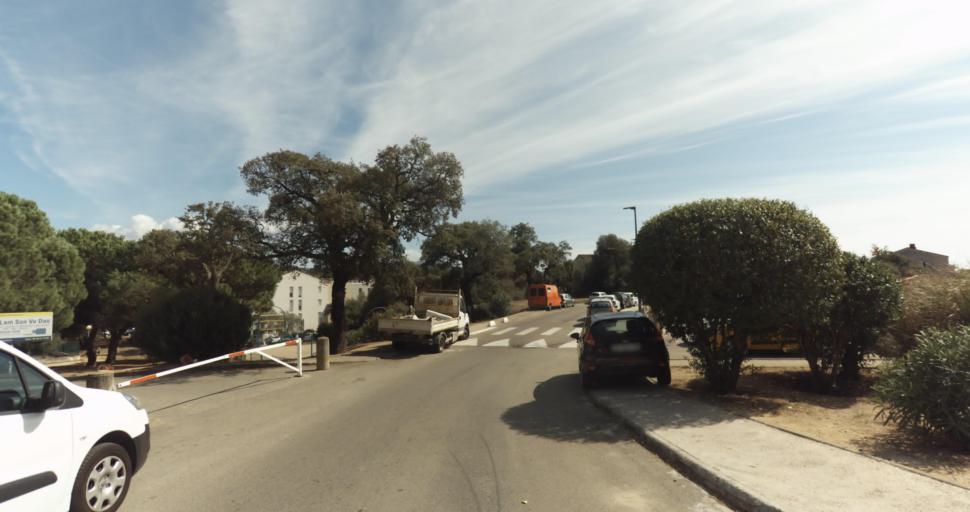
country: FR
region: Corsica
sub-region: Departement de la Corse-du-Sud
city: Ajaccio
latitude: 41.9477
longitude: 8.7537
